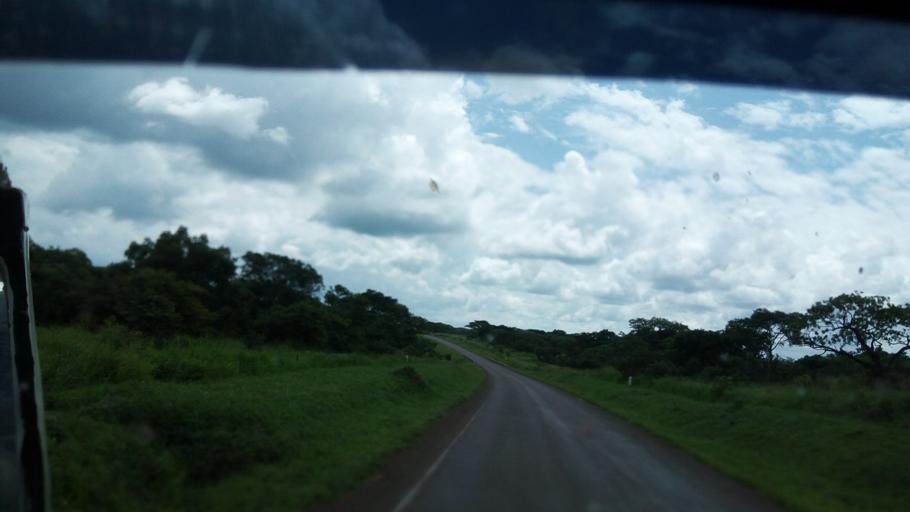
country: UG
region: Northern Region
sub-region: Oyam District
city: Oyam
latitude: 2.3077
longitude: 32.1755
